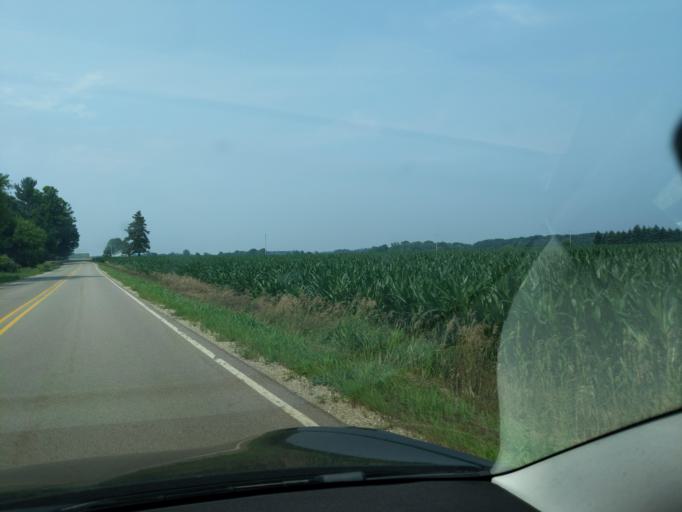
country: US
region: Michigan
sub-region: Clinton County
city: DeWitt
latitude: 42.9126
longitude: -84.5773
